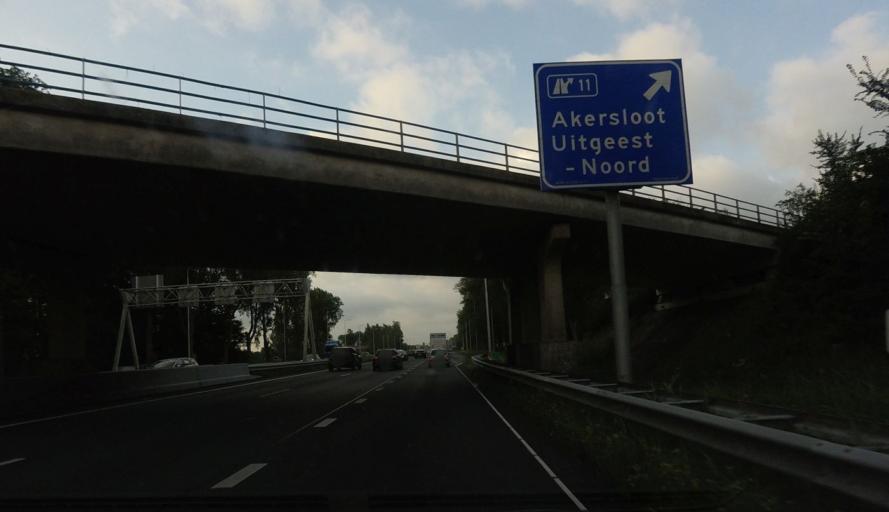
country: NL
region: North Holland
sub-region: Gemeente Uitgeest
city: Uitgeest
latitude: 52.5438
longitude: 4.7200
